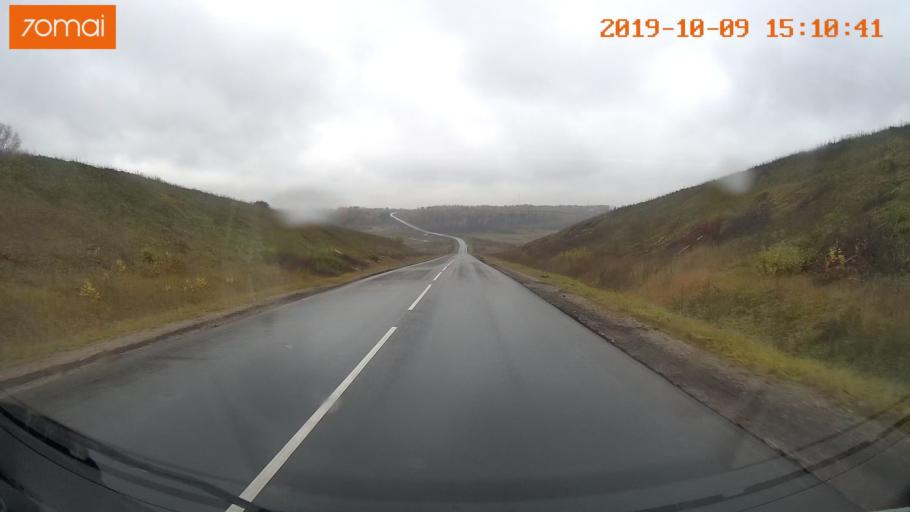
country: RU
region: Kostroma
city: Susanino
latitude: 58.1749
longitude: 41.6374
